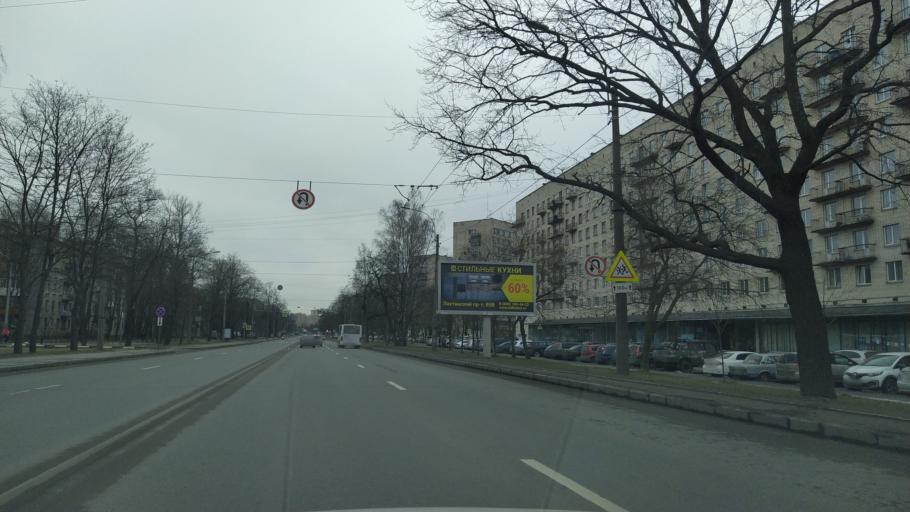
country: RU
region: St.-Petersburg
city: Sosnovka
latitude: 60.0051
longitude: 30.3563
